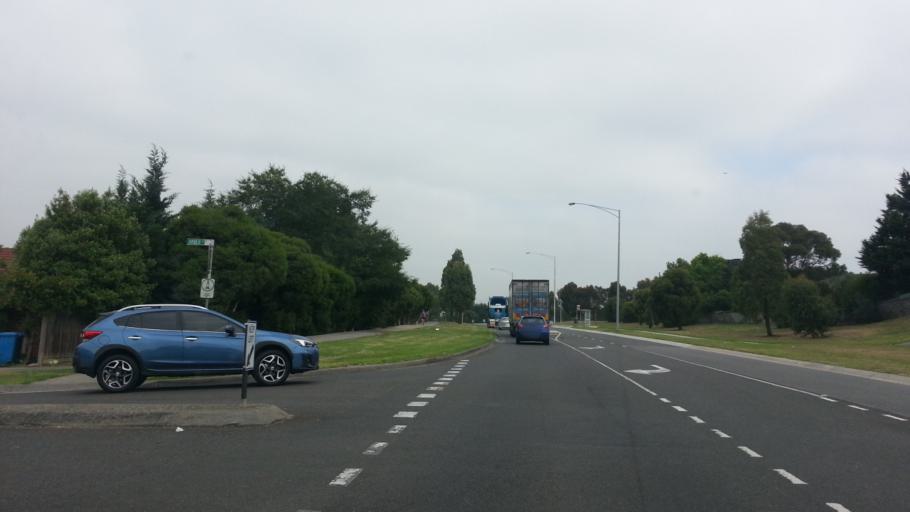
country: AU
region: Victoria
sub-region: Casey
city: Narre Warren North
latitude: -37.9994
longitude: 145.3204
